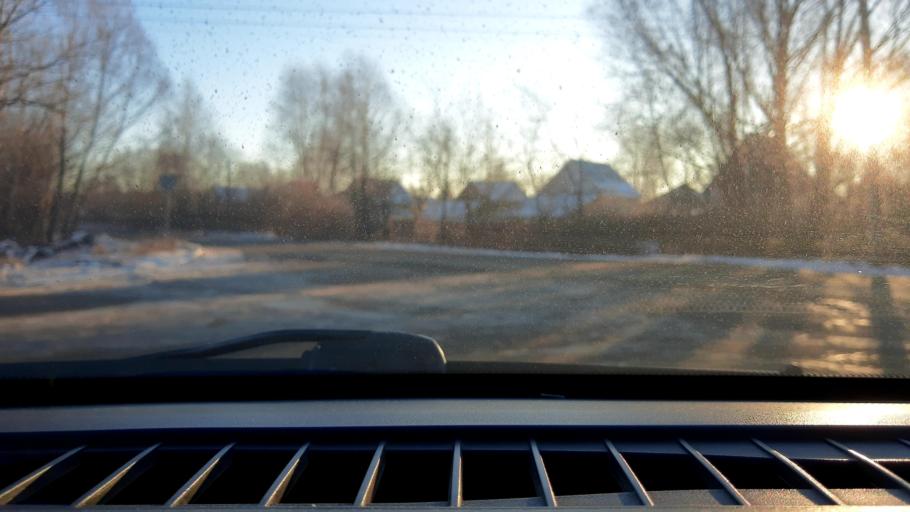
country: RU
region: Nizjnij Novgorod
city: Bor
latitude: 56.3677
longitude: 44.0912
